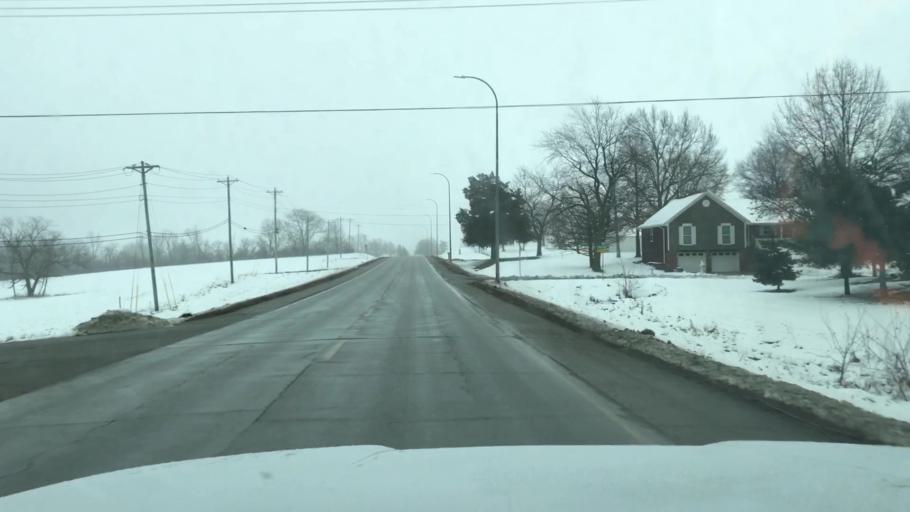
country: US
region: Missouri
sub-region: Clinton County
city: Cameron
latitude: 39.7318
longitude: -94.2328
